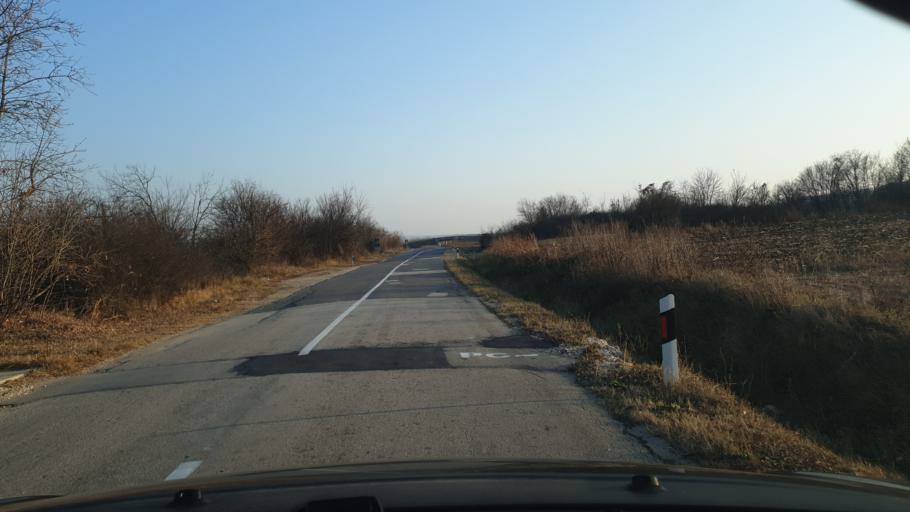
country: RS
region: Central Serbia
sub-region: Zajecarski Okrug
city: Zajecar
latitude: 43.9814
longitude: 22.2894
